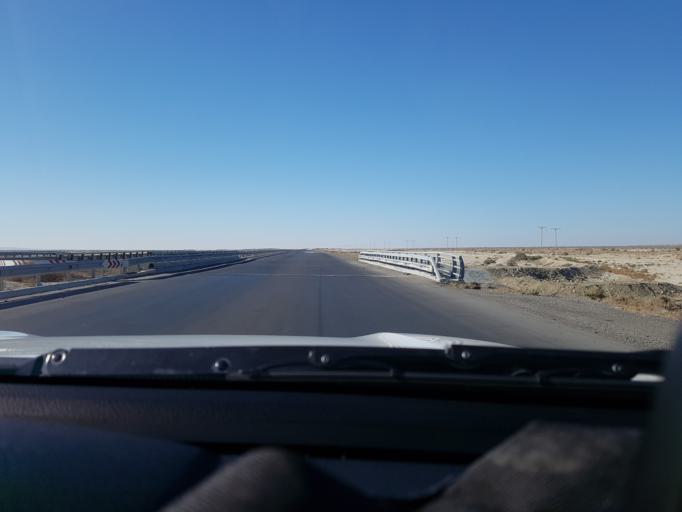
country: TM
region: Balkan
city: Gazanjyk
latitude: 39.2577
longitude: 55.1090
